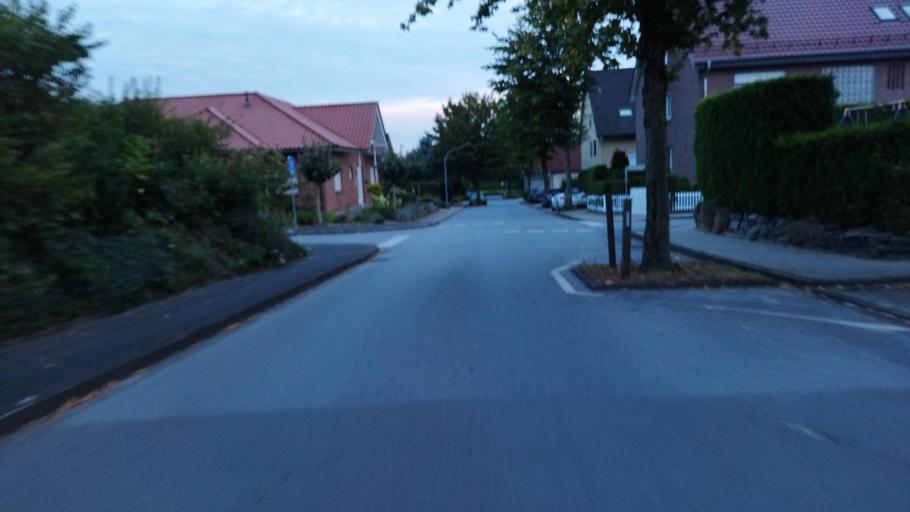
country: DE
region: Lower Saxony
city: Bad Laer
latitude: 52.1036
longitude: 8.0996
